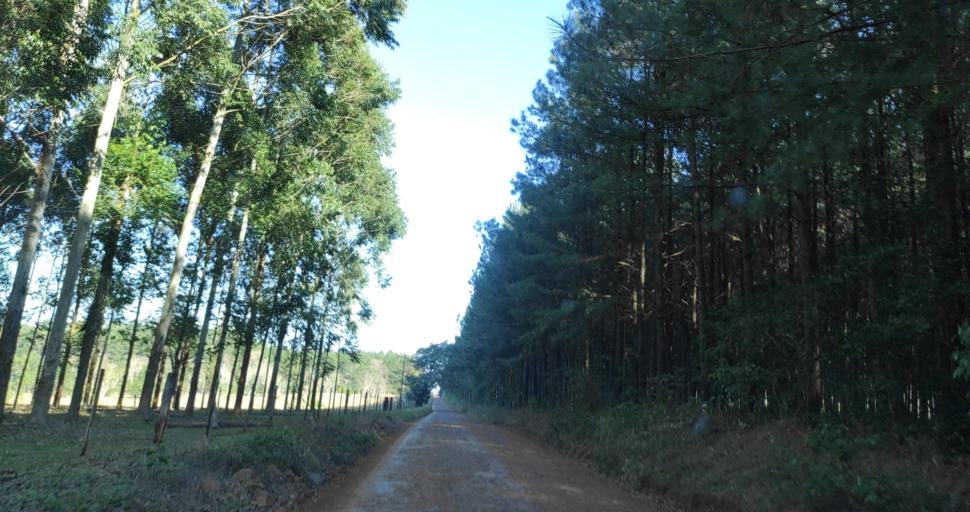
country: AR
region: Misiones
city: Puerto Rico
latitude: -26.8619
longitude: -55.0159
